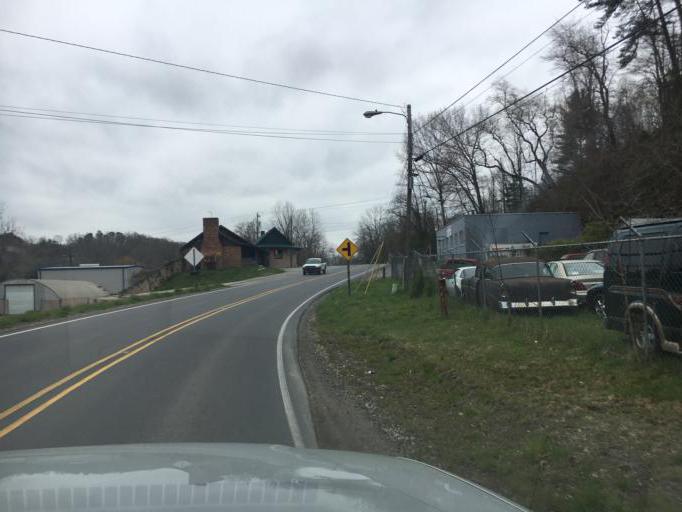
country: US
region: North Carolina
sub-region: Buncombe County
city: Woodfin
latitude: 35.6270
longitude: -82.6007
